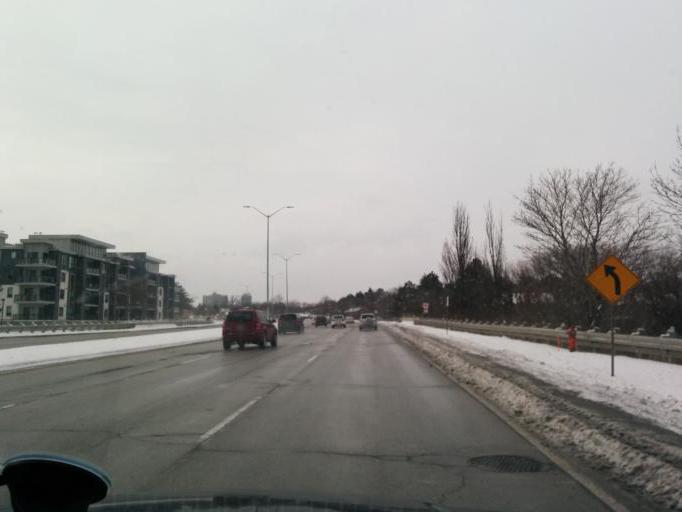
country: CA
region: Ontario
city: Mississauga
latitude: 43.5392
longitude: -79.6693
